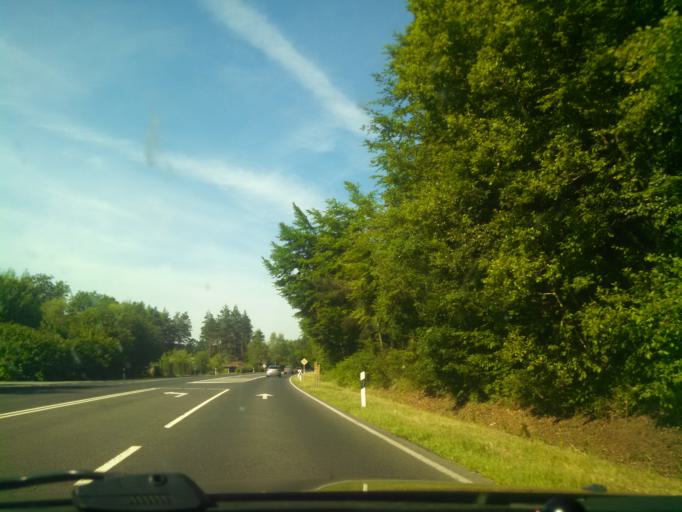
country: LU
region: Grevenmacher
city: Gonderange
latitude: 49.6753
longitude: 6.2153
